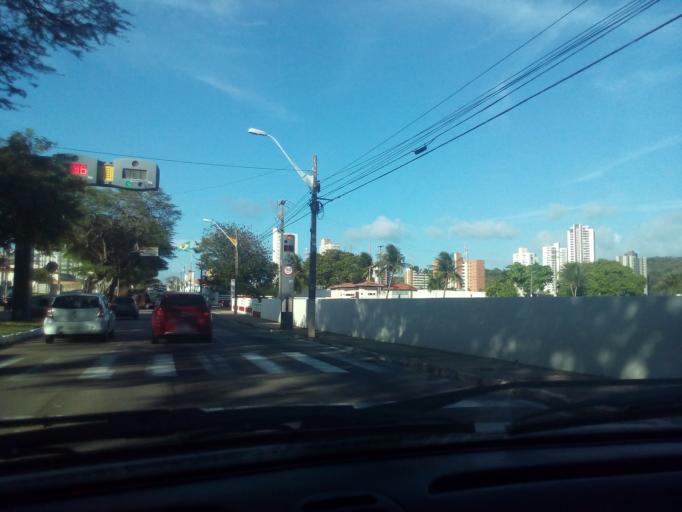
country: BR
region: Rio Grande do Norte
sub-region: Natal
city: Natal
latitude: -5.8037
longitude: -35.2017
